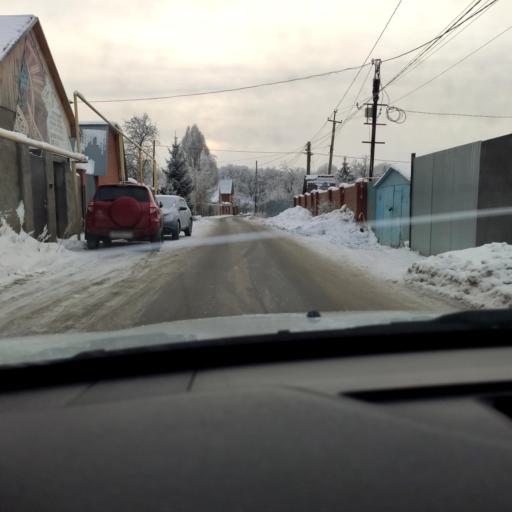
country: RU
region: Samara
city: Petra-Dubrava
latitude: 53.2974
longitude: 50.2479
